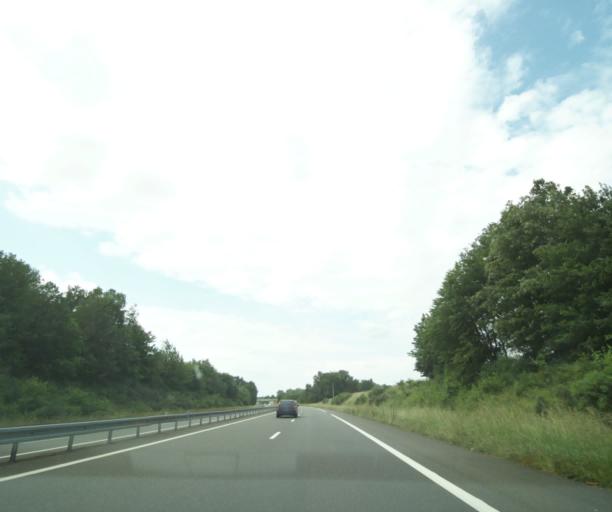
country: FR
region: Pays de la Loire
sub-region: Departement de Maine-et-Loire
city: Brion
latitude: 47.4502
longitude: -0.1771
